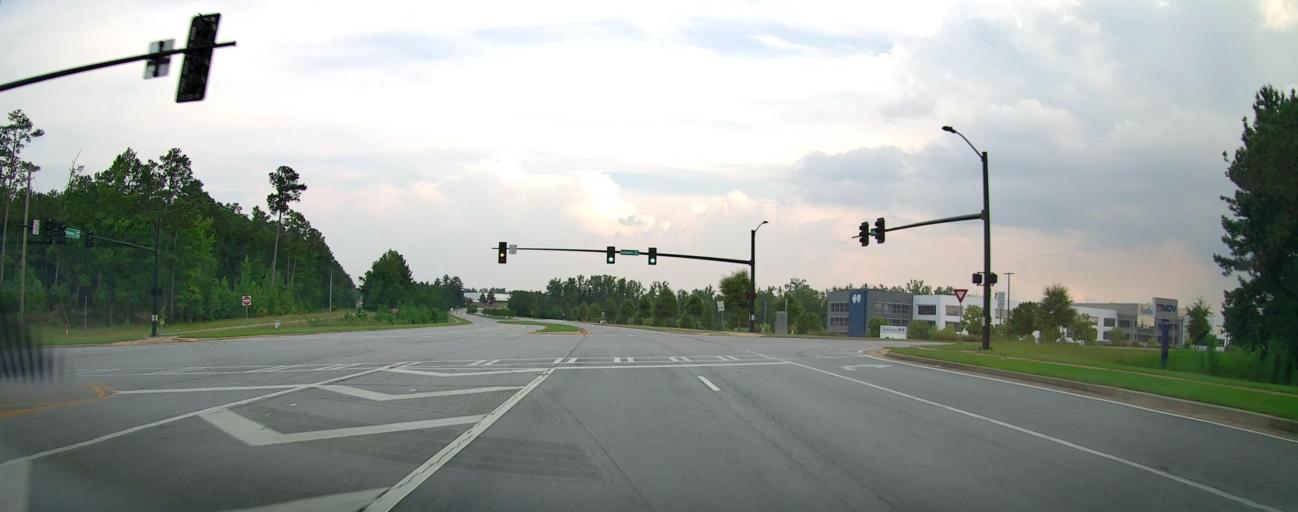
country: US
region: Georgia
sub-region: Muscogee County
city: Columbus
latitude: 32.5316
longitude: -84.8408
